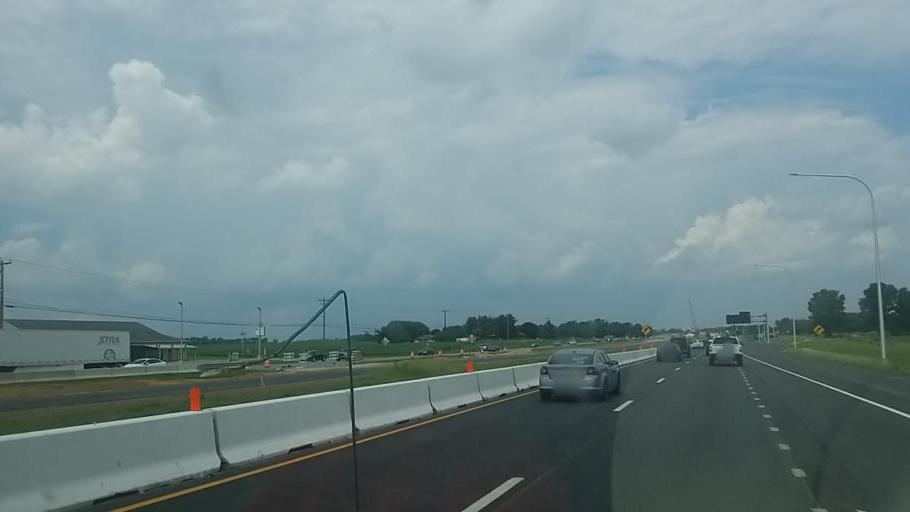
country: US
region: Delaware
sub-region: Kent County
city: Riverview
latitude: 39.0322
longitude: -75.4581
